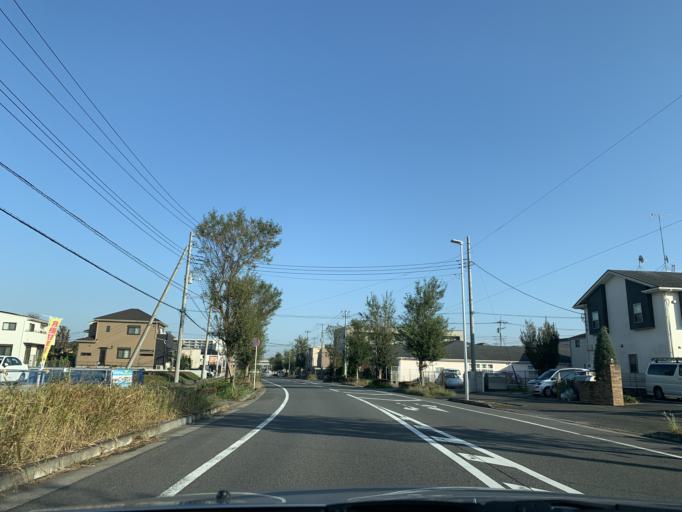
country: JP
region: Ibaraki
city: Moriya
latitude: 35.9135
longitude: 139.9532
